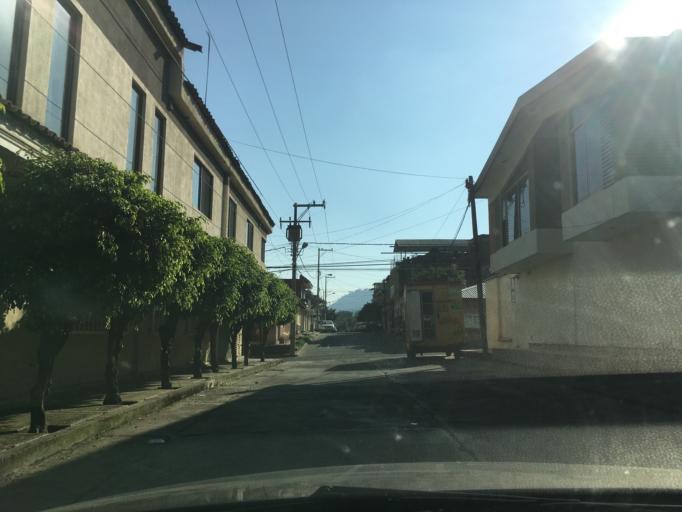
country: MX
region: Michoacan
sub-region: Uruapan
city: Uruapan
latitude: 19.4159
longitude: -102.0679
